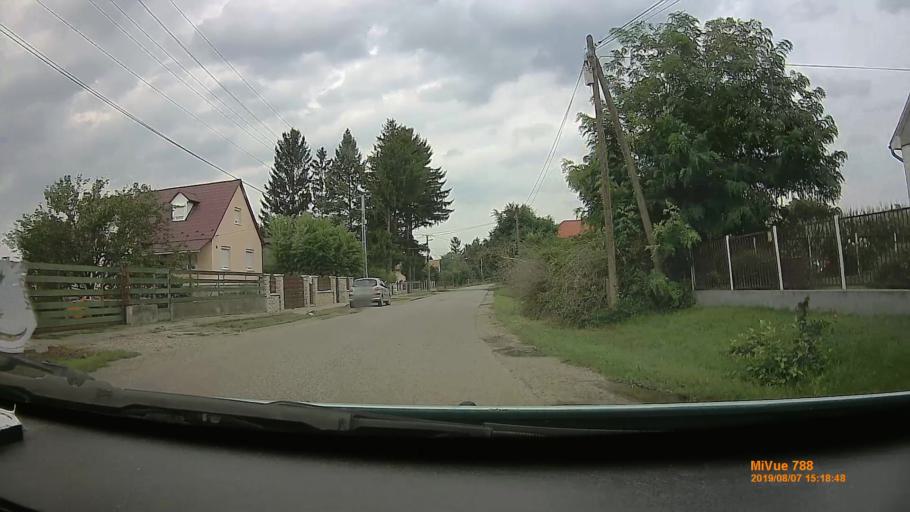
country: HU
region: Borsod-Abauj-Zemplen
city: Encs
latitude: 48.3468
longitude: 21.1399
